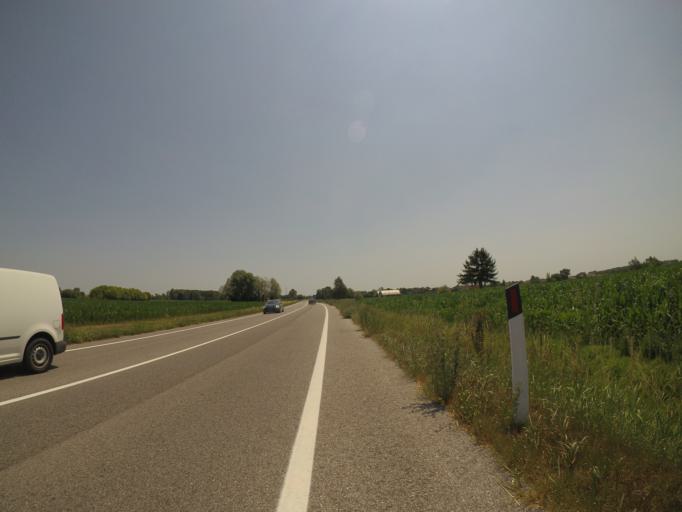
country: IT
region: Friuli Venezia Giulia
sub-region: Provincia di Udine
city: Varmo
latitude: 45.8993
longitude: 13.0070
